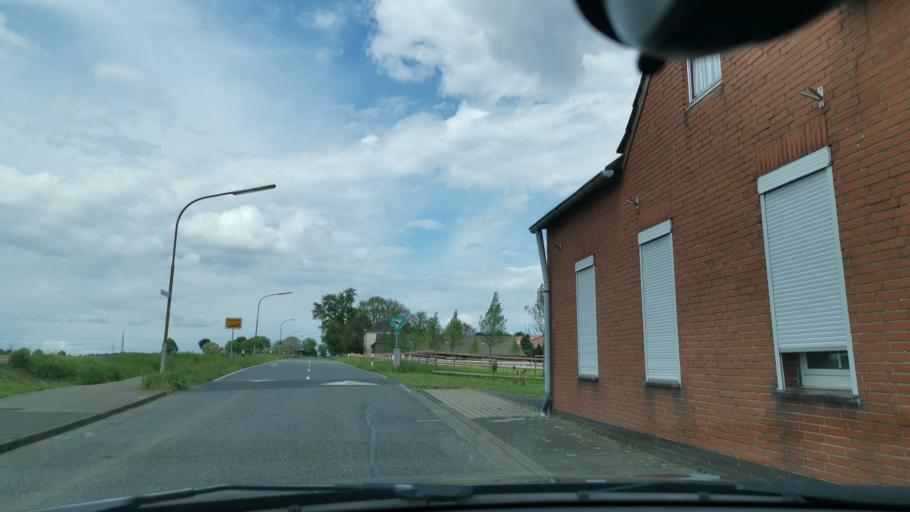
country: DE
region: North Rhine-Westphalia
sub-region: Regierungsbezirk Dusseldorf
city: Rommerskirchen
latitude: 51.0753
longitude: 6.6907
